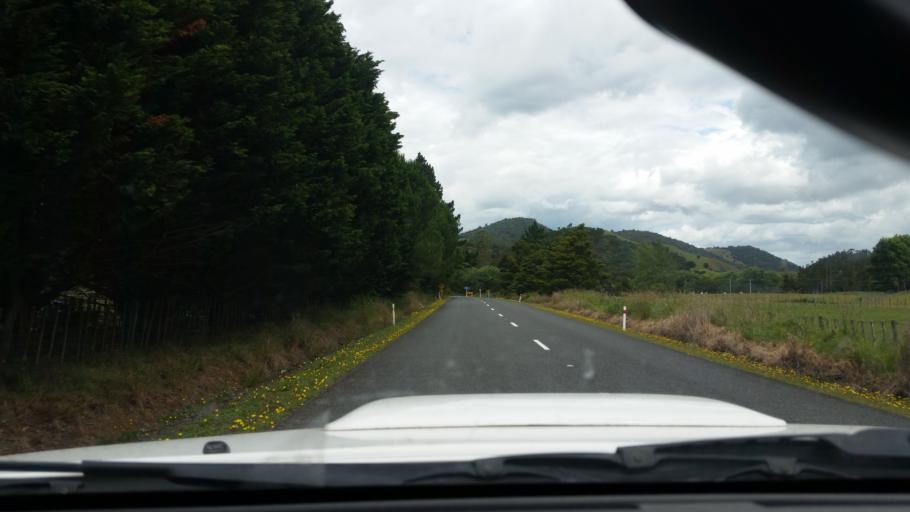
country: NZ
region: Northland
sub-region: Kaipara District
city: Dargaville
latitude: -35.7513
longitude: 173.9003
